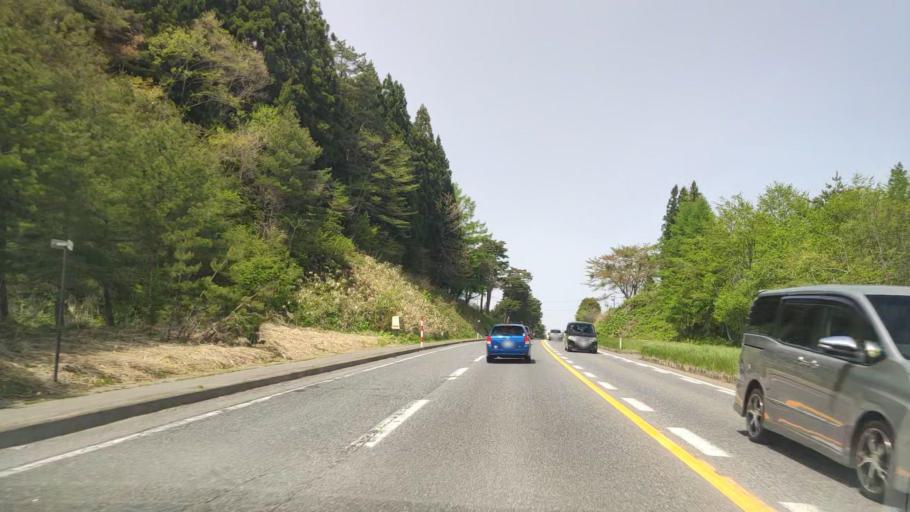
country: JP
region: Aomori
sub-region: Misawa Shi
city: Inuotose
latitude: 40.6664
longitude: 141.1859
